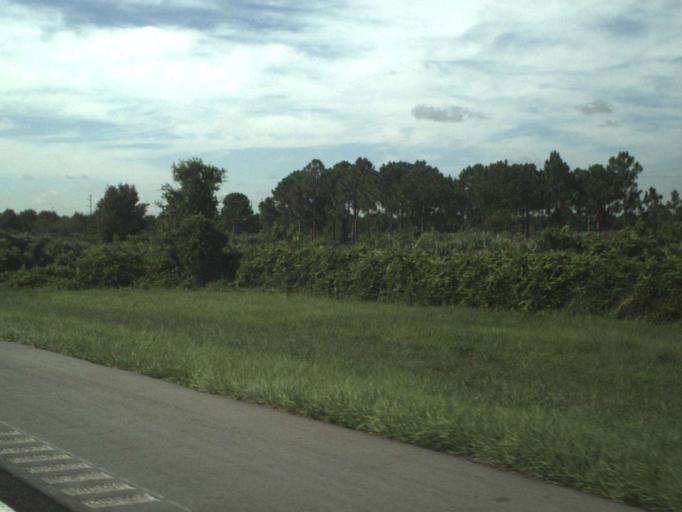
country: US
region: Florida
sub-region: Indian River County
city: West Vero Corridor
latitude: 27.5755
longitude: -80.4939
